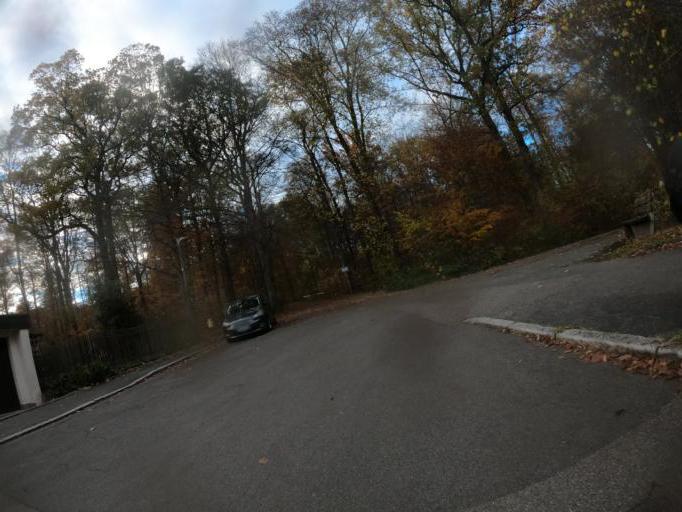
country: DE
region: Baden-Wuerttemberg
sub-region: Regierungsbezirk Stuttgart
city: Sindelfingen
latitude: 48.7104
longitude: 9.0322
